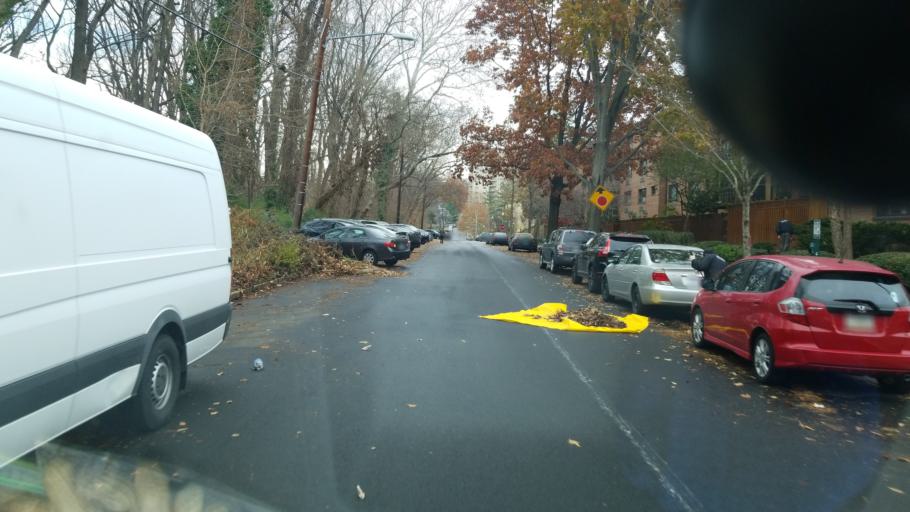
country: US
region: Maryland
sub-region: Montgomery County
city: Friendship Village
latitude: 38.9225
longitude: -77.0820
